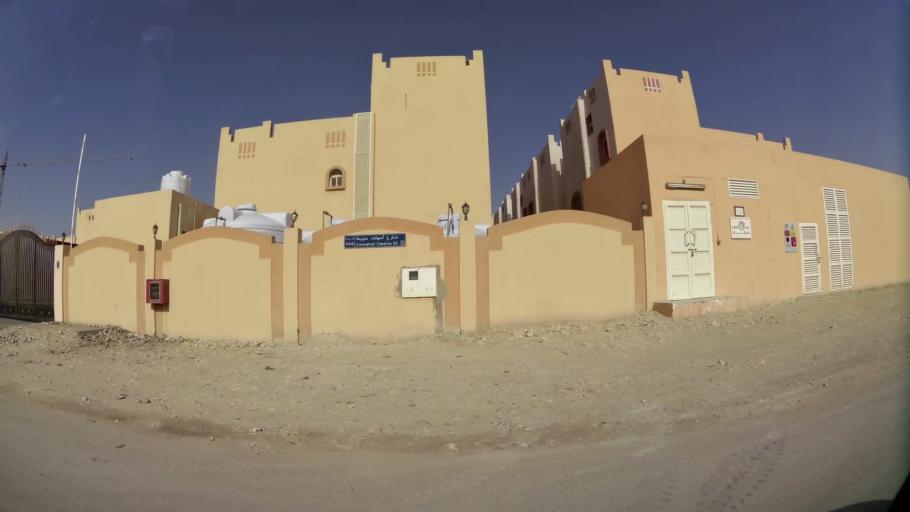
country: QA
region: Baladiyat ar Rayyan
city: Ar Rayyan
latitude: 25.3450
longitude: 51.4286
